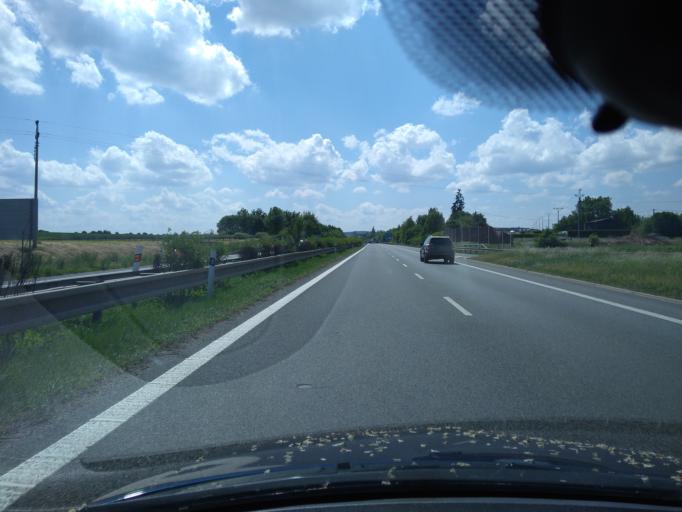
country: CZ
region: Plzensky
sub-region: Okres Plzen-Mesto
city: Pilsen
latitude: 49.7088
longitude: 13.3625
